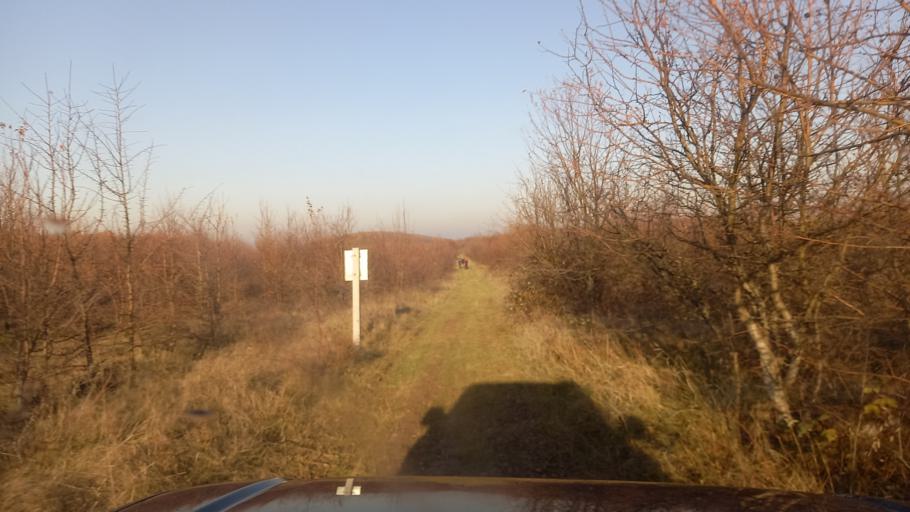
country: RU
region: Krasnodarskiy
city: Azovskaya
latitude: 44.8080
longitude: 38.5933
